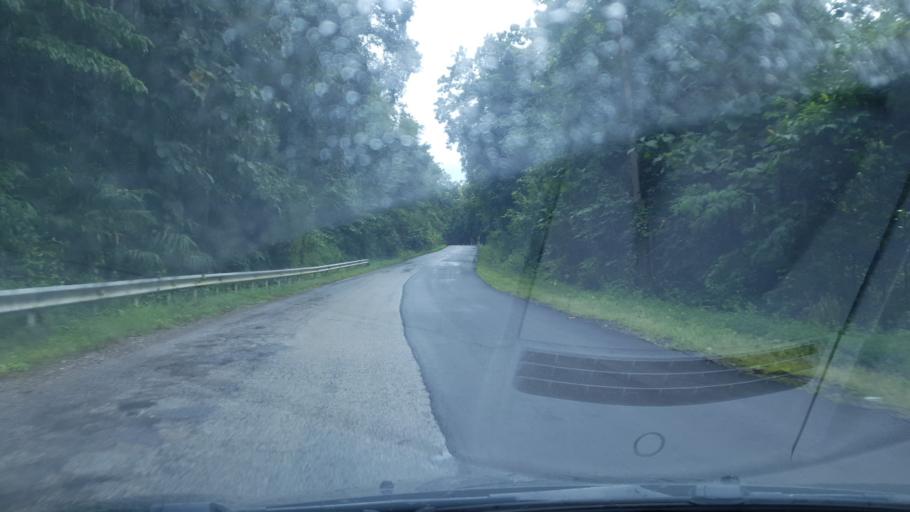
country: TH
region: Mae Hong Son
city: Pa Pae
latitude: 18.2744
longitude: 97.9388
